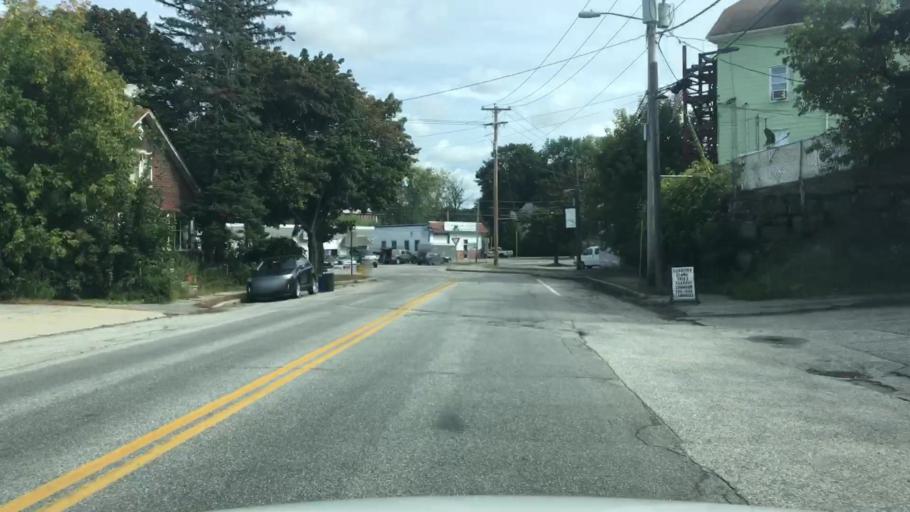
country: US
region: Maine
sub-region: Androscoggin County
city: Auburn
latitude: 44.0874
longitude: -70.2217
